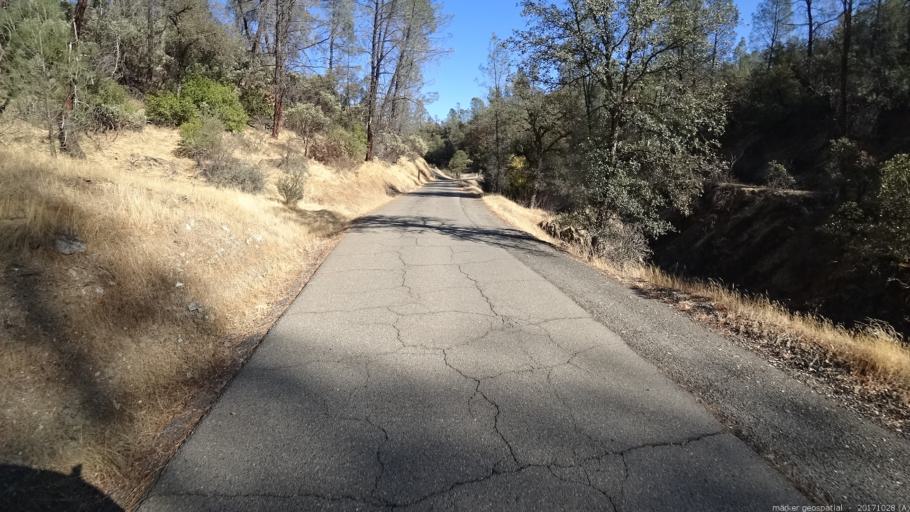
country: US
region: California
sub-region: Shasta County
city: Shasta
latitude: 40.5946
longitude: -122.4563
